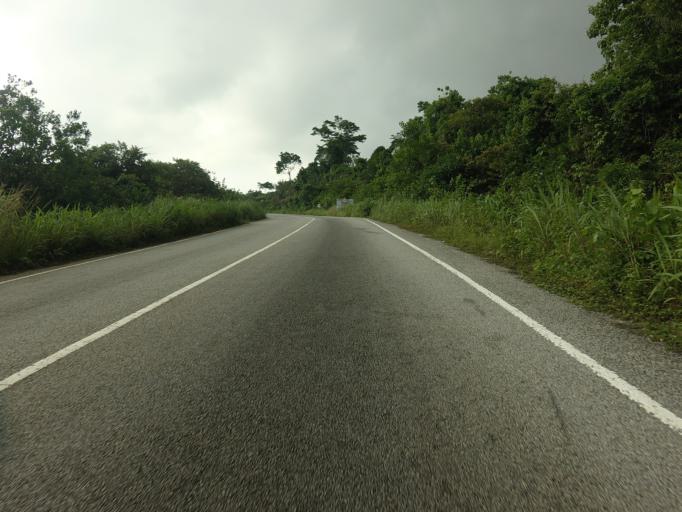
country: GH
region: Volta
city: Ho
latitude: 6.8132
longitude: 0.4207
